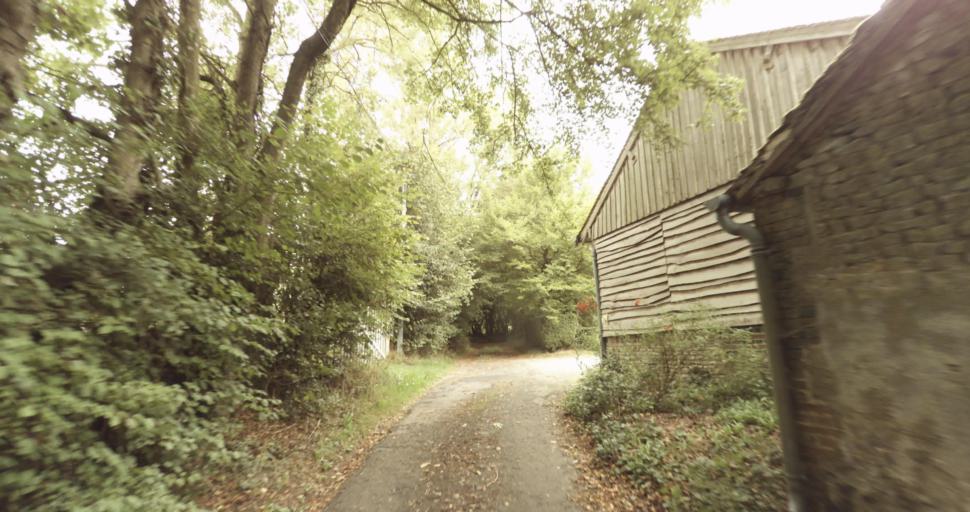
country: FR
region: Lower Normandy
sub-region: Departement de l'Orne
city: Gace
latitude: 48.6813
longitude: 0.3031
